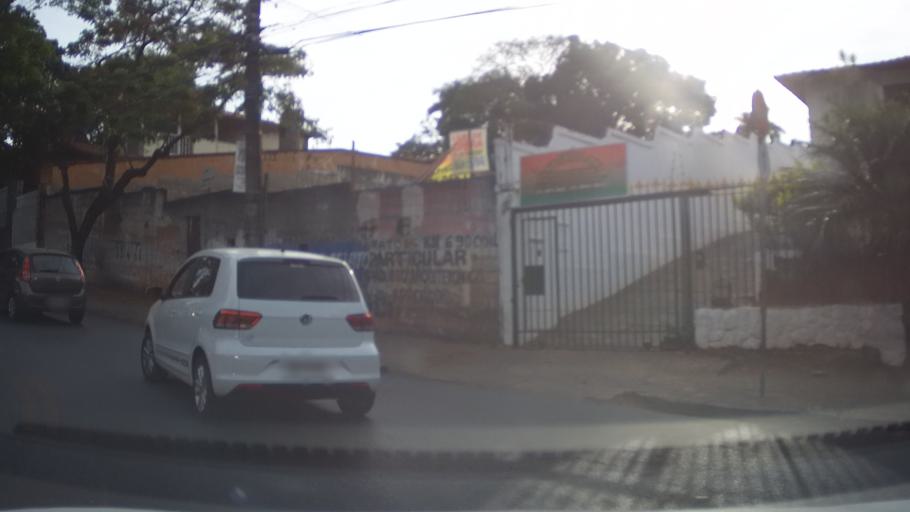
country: BR
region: Minas Gerais
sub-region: Belo Horizonte
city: Belo Horizonte
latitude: -19.8594
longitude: -43.9898
